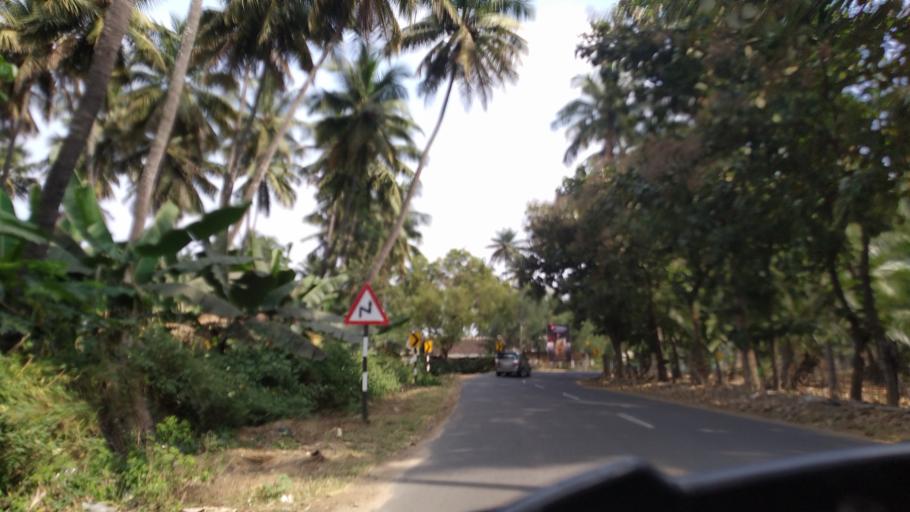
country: IN
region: Tamil Nadu
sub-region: Coimbatore
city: Perur
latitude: 10.9547
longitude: 76.7613
